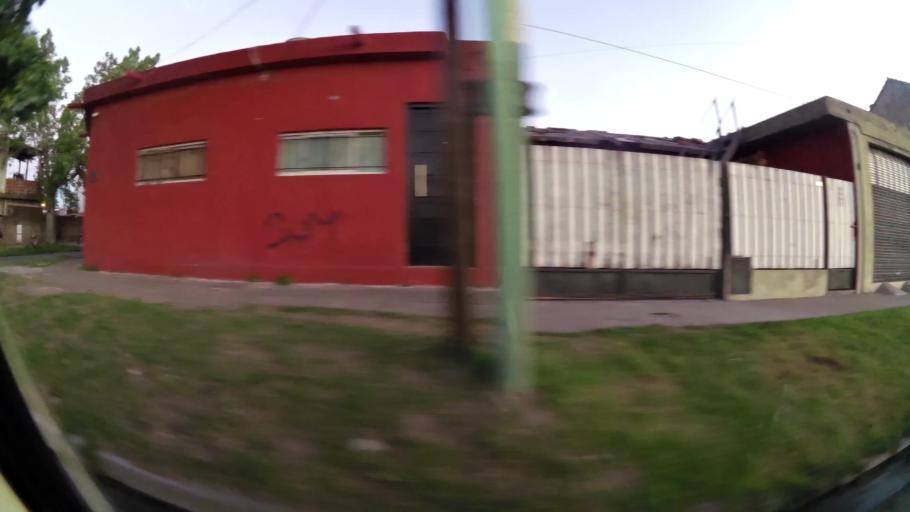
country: AR
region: Buenos Aires
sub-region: Partido de Quilmes
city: Quilmes
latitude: -34.8011
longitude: -58.1756
